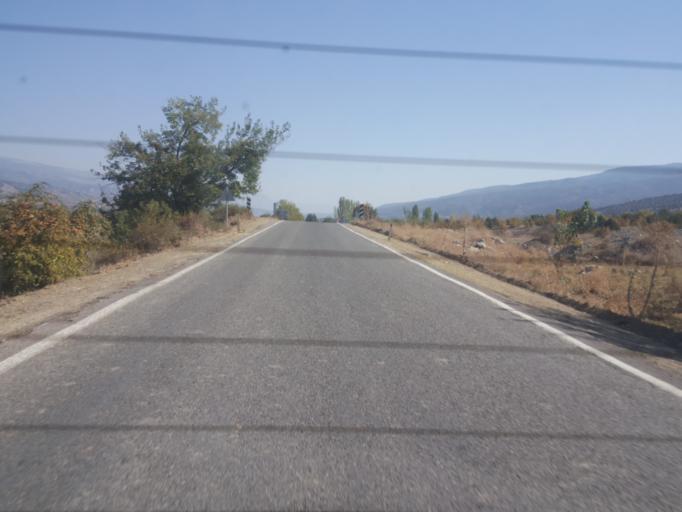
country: TR
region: Kastamonu
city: Tosya
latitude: 40.9918
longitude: 34.1149
